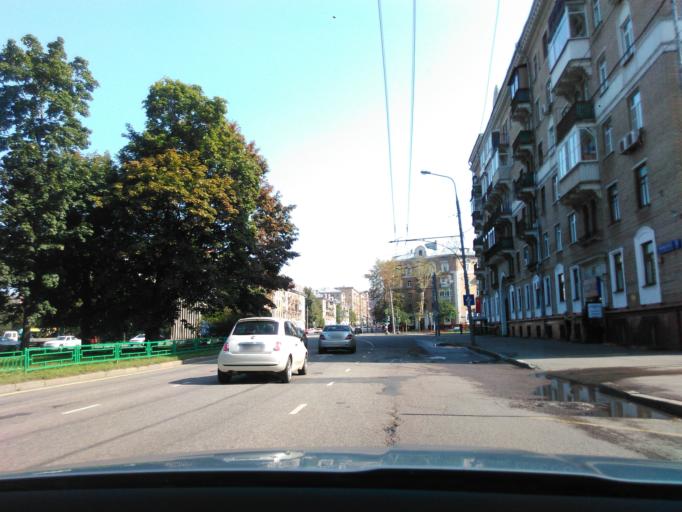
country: RU
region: Moscow
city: Sokol
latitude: 55.7986
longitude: 37.5150
